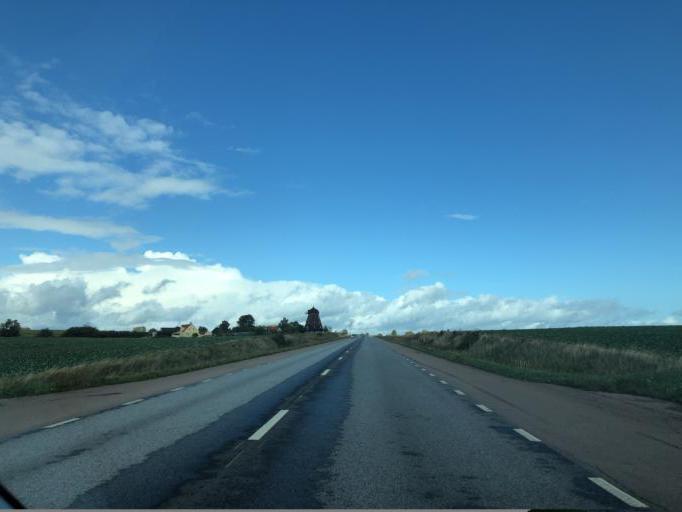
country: SE
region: Skane
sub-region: Landskrona
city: Landskrona
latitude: 55.9091
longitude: 12.8256
